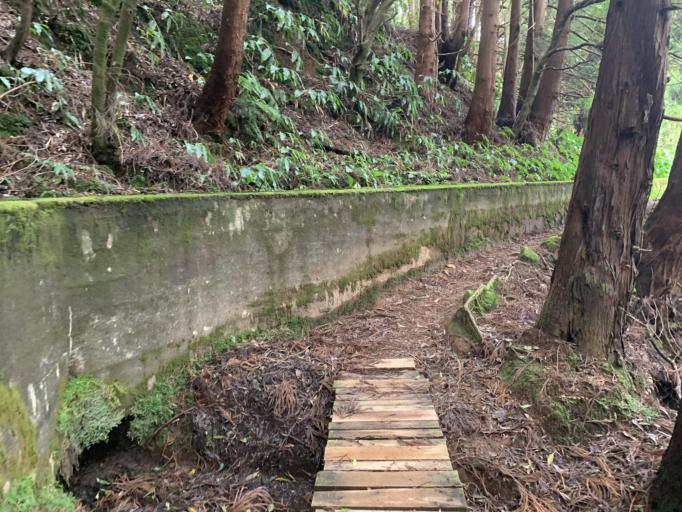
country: PT
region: Azores
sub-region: Vila Franca do Campo
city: Vila Franca do Campo
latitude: 37.7444
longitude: -25.4755
